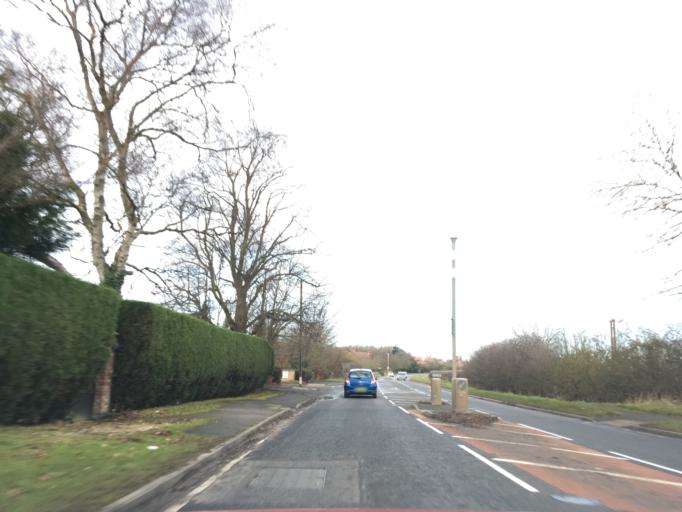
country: GB
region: England
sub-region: Nottinghamshire
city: Ruddington
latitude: 52.8686
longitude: -1.1307
